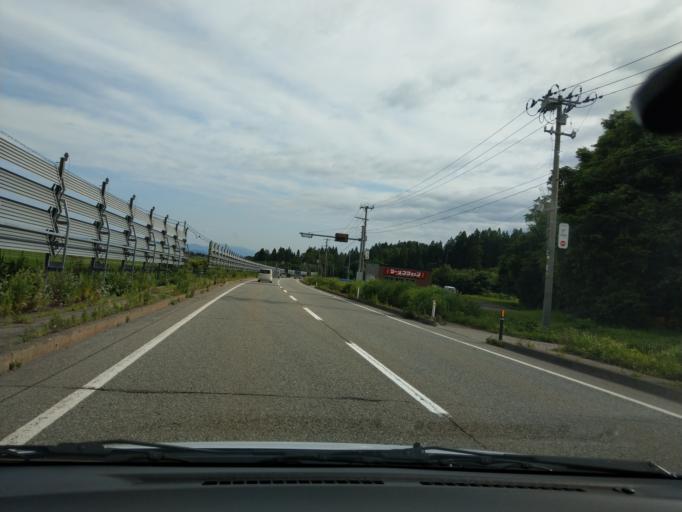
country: JP
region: Akita
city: Yokotemachi
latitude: 39.3842
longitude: 140.5677
